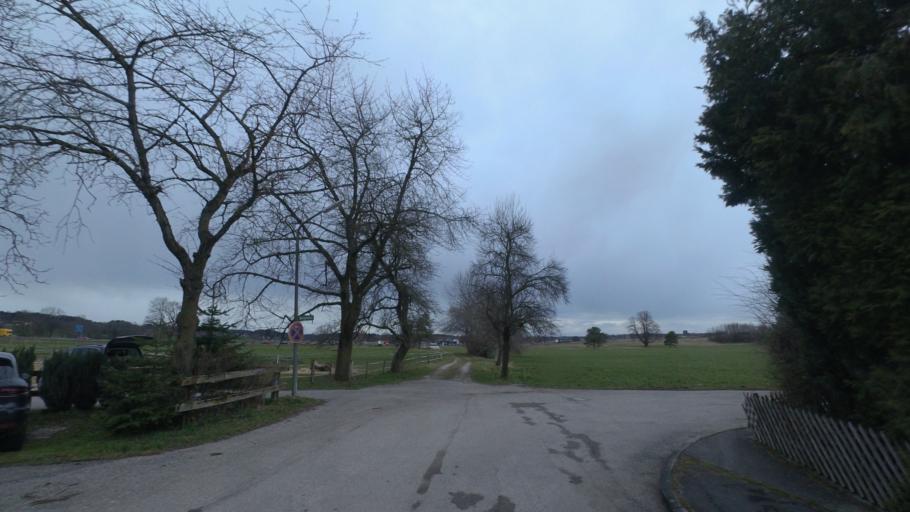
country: DE
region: Bavaria
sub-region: Upper Bavaria
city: Bernau am Chiemsee
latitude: 47.8147
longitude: 12.3713
